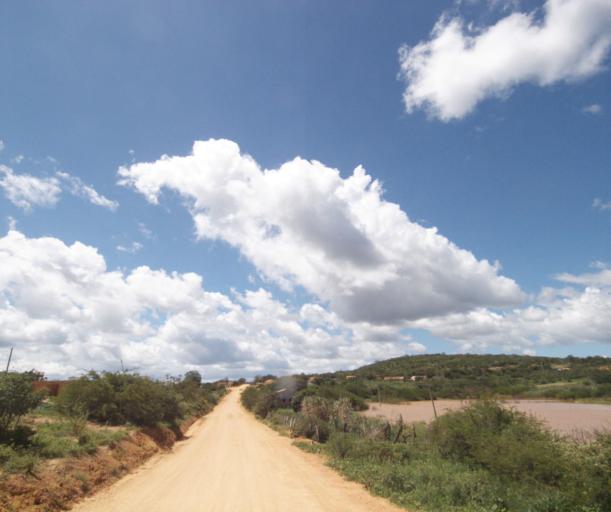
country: BR
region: Bahia
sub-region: Pocoes
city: Pocoes
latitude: -14.3348
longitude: -40.5959
